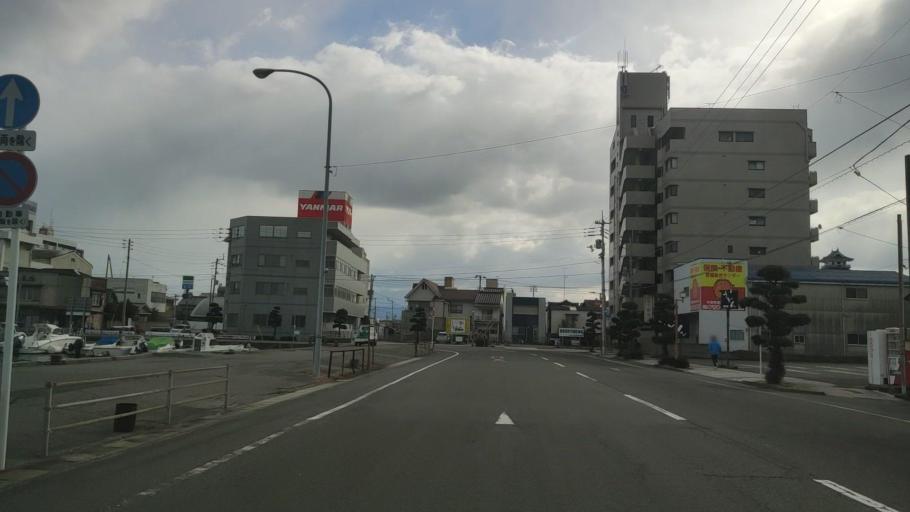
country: JP
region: Ehime
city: Saijo
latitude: 34.0664
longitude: 133.0063
